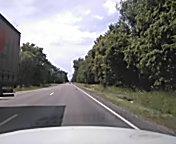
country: LT
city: Vilkaviskis
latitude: 54.6364
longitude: 22.9806
